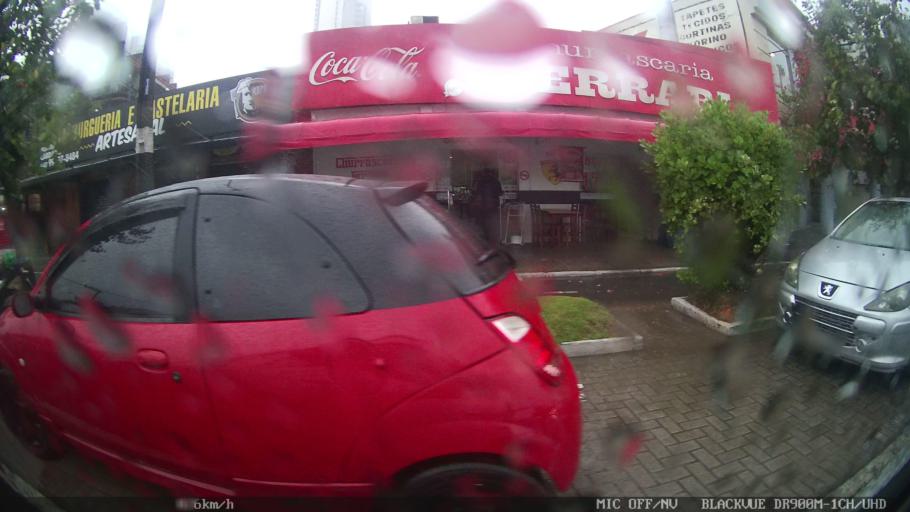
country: BR
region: Santa Catarina
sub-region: Balneario Camboriu
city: Balneario Camboriu
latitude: -26.9856
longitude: -48.6397
